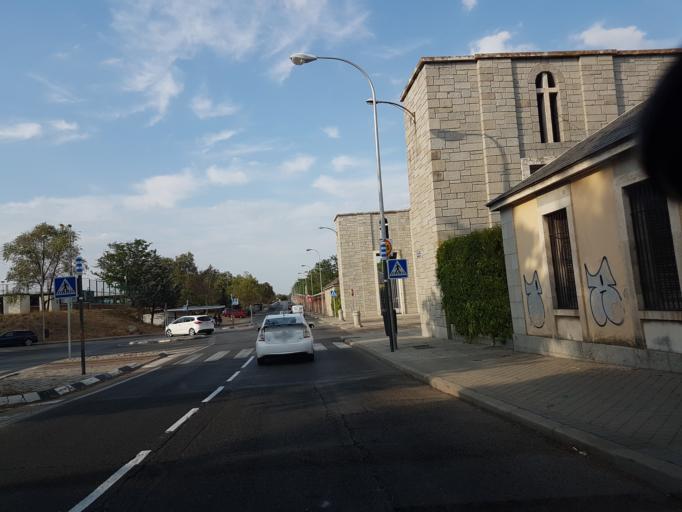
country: ES
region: Madrid
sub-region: Provincia de Madrid
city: Moratalaz
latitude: 40.4181
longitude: -3.6494
